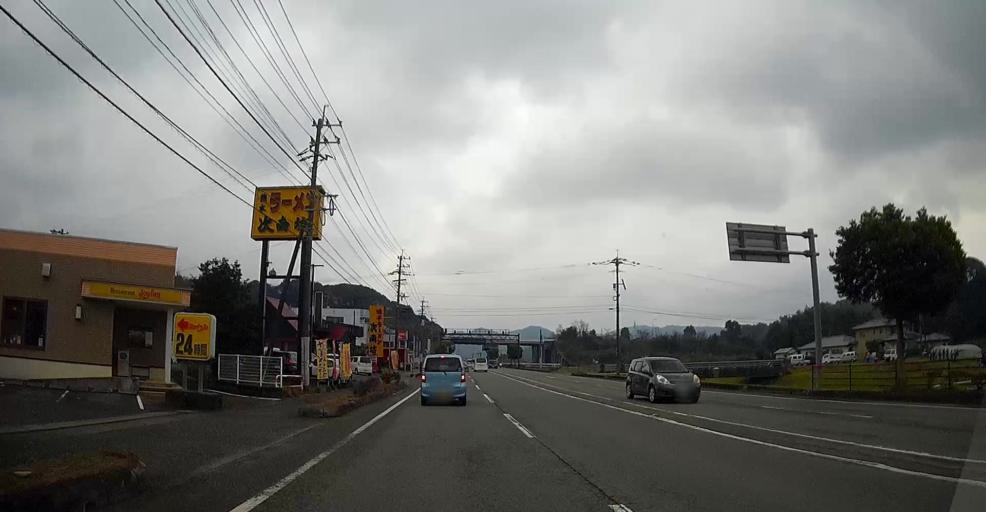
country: JP
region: Kumamoto
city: Matsubase
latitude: 32.6513
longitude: 130.7072
